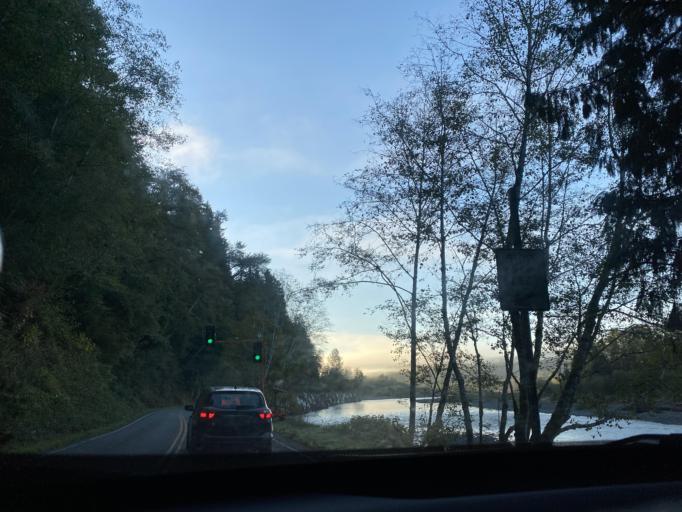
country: US
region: Washington
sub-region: Clallam County
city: Forks
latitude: 47.8226
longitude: -124.1841
